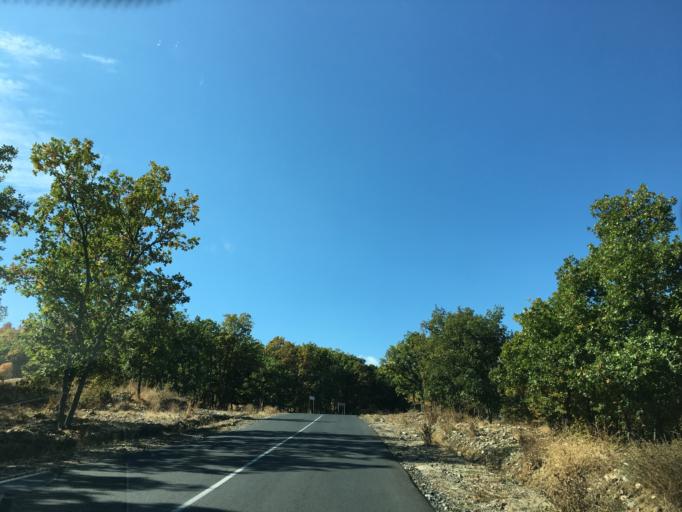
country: BG
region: Kurdzhali
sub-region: Obshtina Krumovgrad
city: Krumovgrad
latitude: 41.4740
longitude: 25.5453
